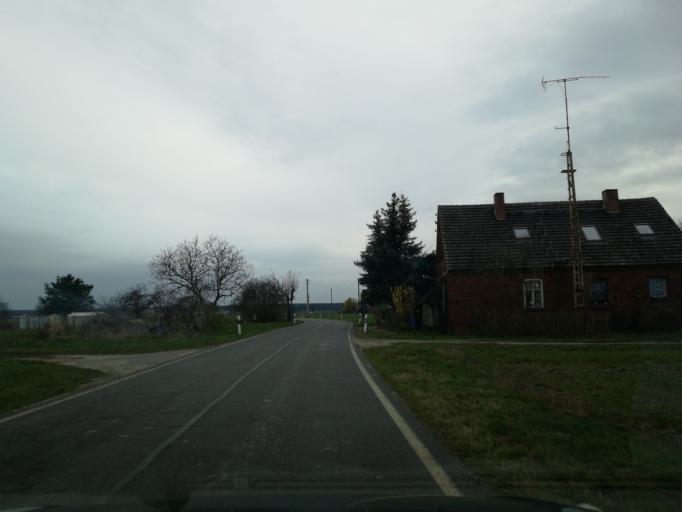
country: DE
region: Brandenburg
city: Vetschau
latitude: 51.7427
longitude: 14.0257
